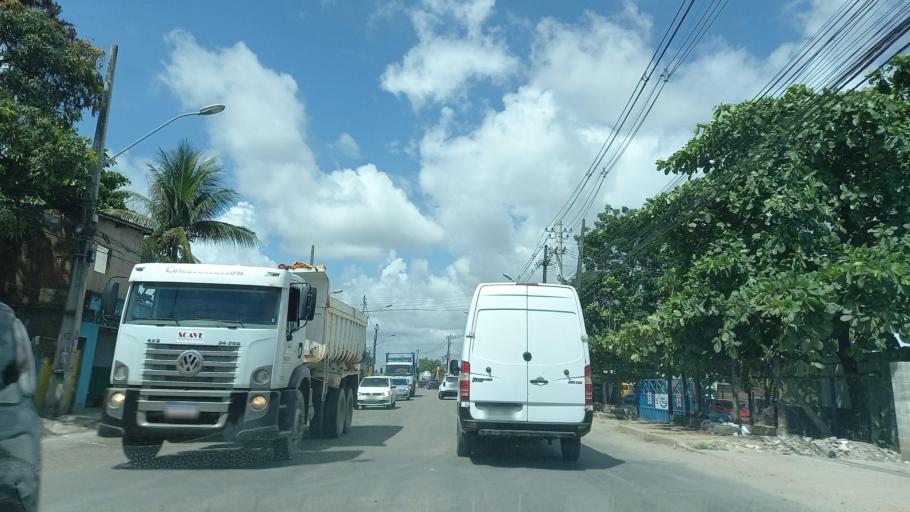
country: BR
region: Pernambuco
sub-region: Jaboatao Dos Guararapes
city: Jaboatao
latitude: -8.1537
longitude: -34.9576
